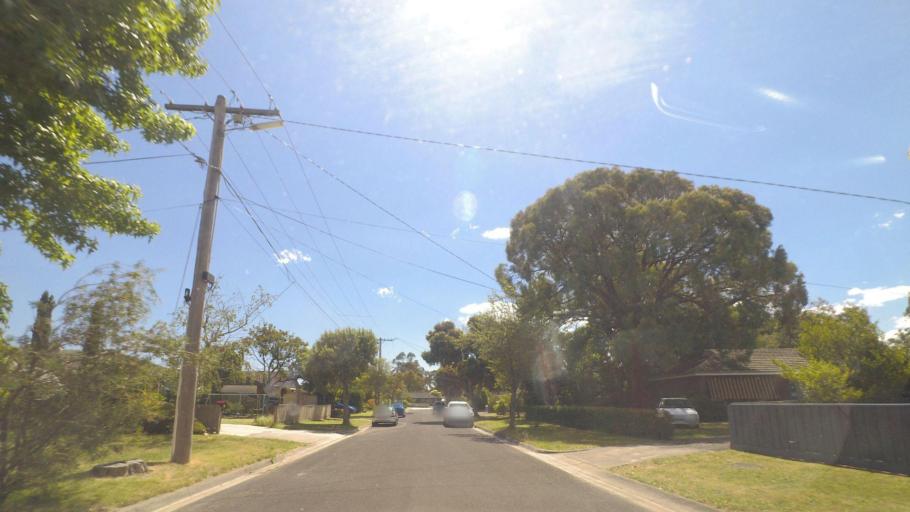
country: AU
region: Victoria
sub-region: Yarra Ranges
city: Kilsyth
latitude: -37.8090
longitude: 145.3146
